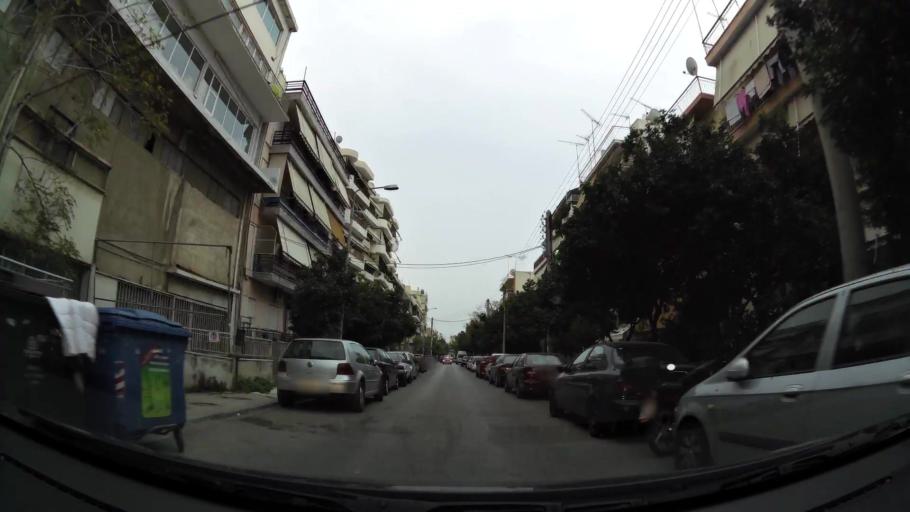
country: GR
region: Attica
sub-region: Nomos Piraios
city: Agios Ioannis Rentis
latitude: 37.9637
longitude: 23.6766
